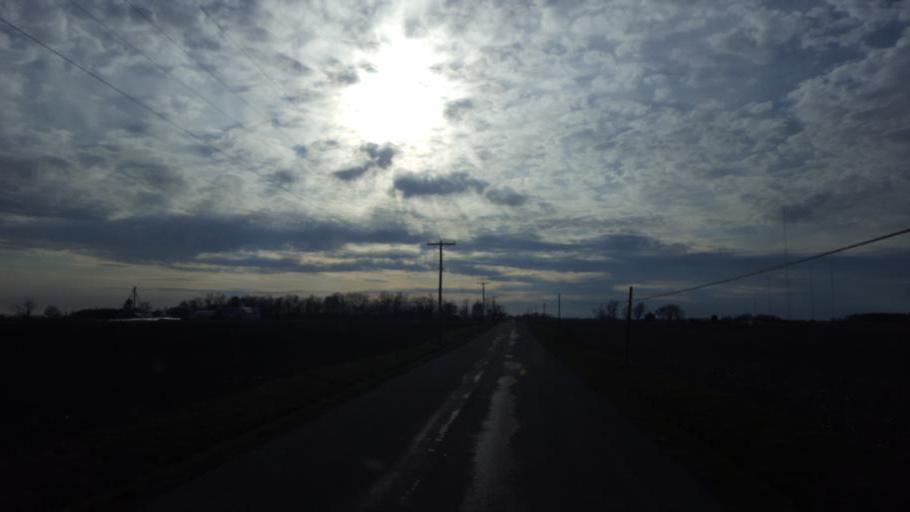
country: US
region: Ohio
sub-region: Crawford County
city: Bucyrus
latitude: 40.7618
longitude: -82.9265
